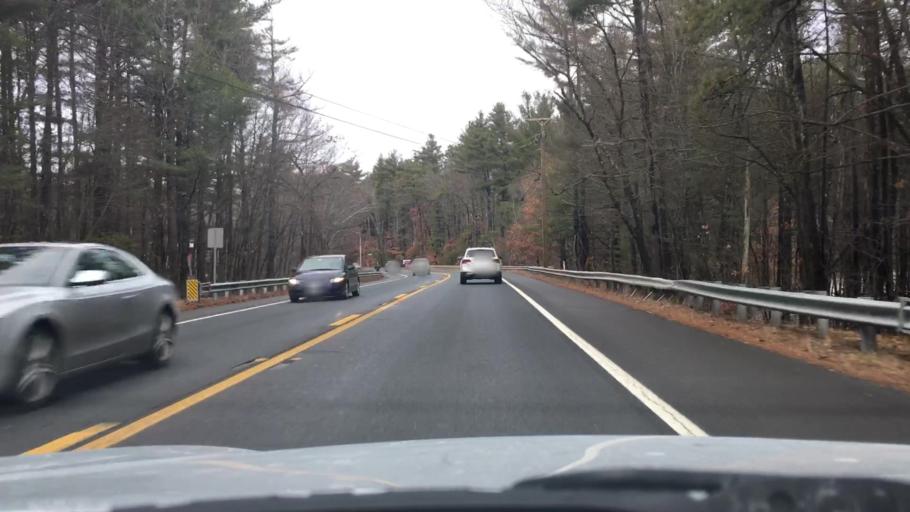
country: US
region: Massachusetts
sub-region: Franklin County
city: Millers Falls
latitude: 42.6051
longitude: -72.5030
